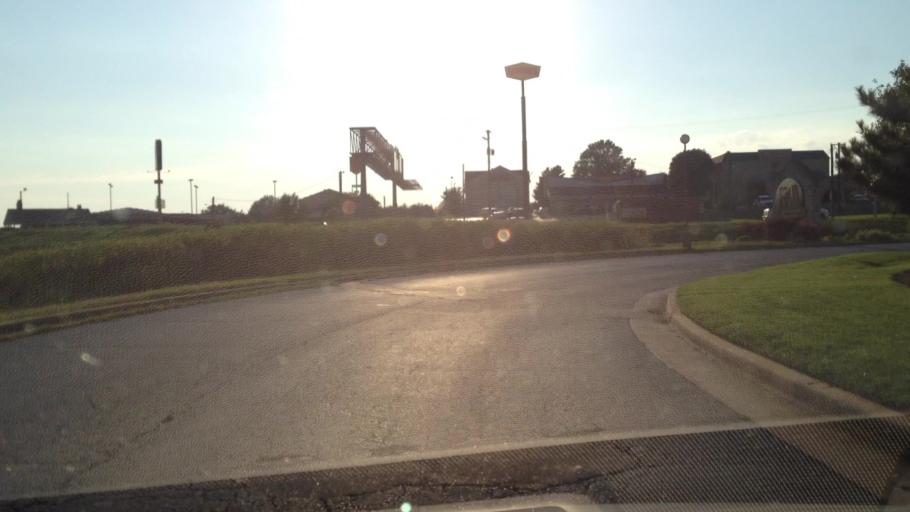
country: US
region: Missouri
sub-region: Jasper County
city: Duquesne
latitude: 37.0489
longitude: -94.4774
